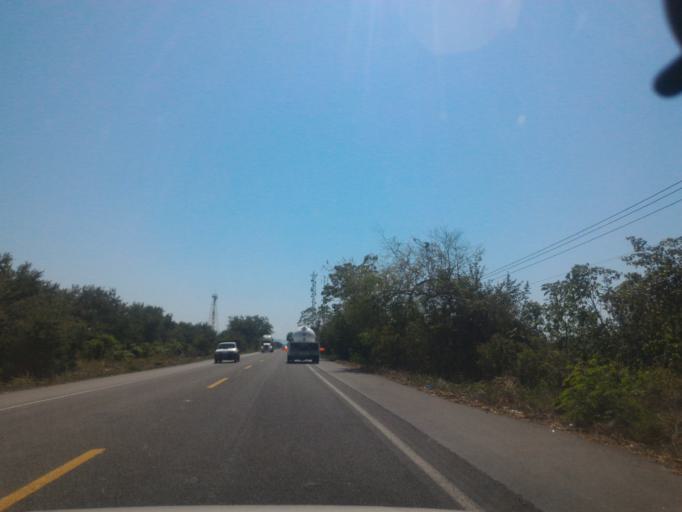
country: MX
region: Colima
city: Tecoman
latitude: 18.8315
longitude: -103.8166
